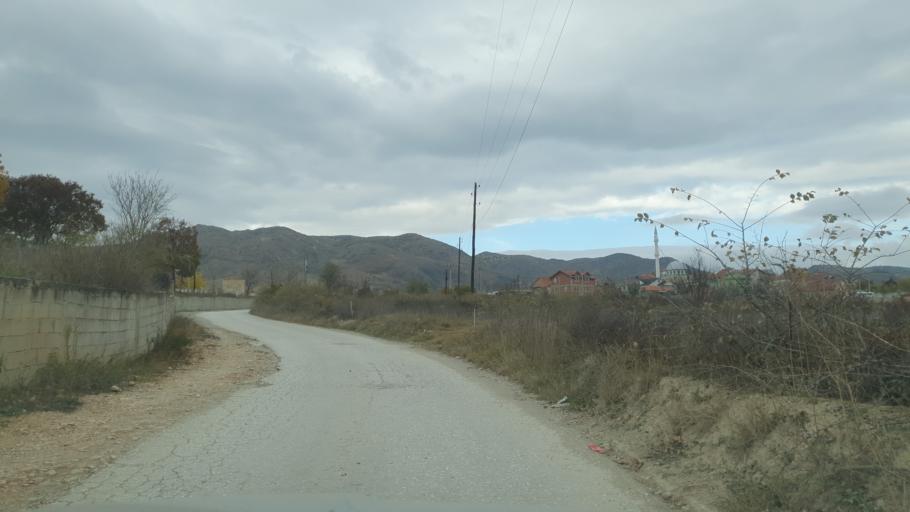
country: MK
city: Kondovo
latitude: 42.0392
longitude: 21.2800
